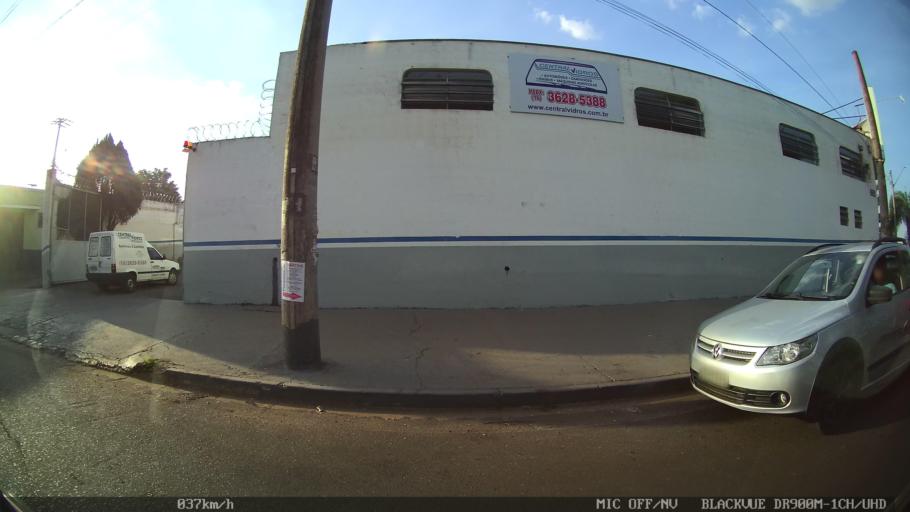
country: BR
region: Sao Paulo
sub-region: Ribeirao Preto
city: Ribeirao Preto
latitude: -21.1375
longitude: -47.7987
